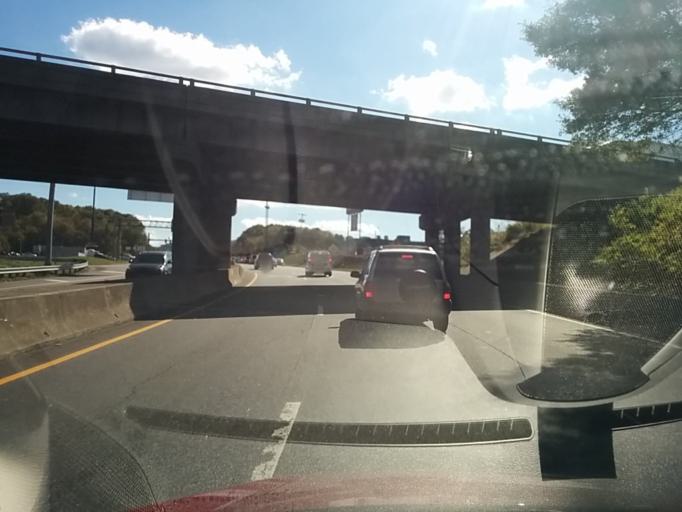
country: US
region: Virginia
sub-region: Botetourt County
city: Daleville
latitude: 37.3884
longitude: -79.9049
